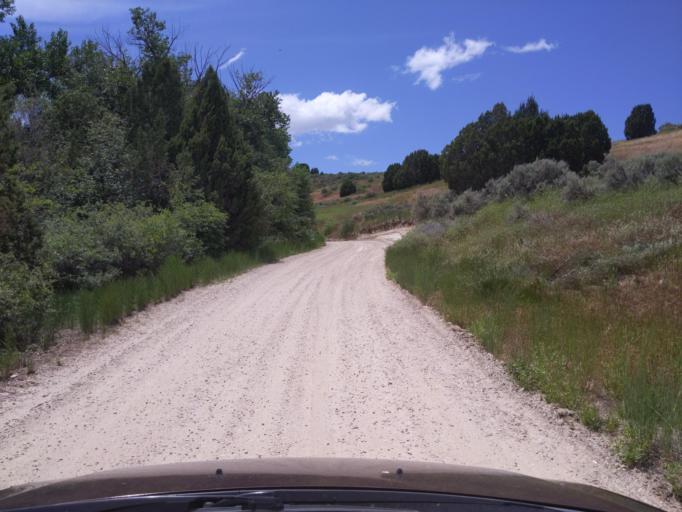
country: US
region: Idaho
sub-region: Bannock County
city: Pocatello
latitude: 42.8411
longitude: -112.4625
